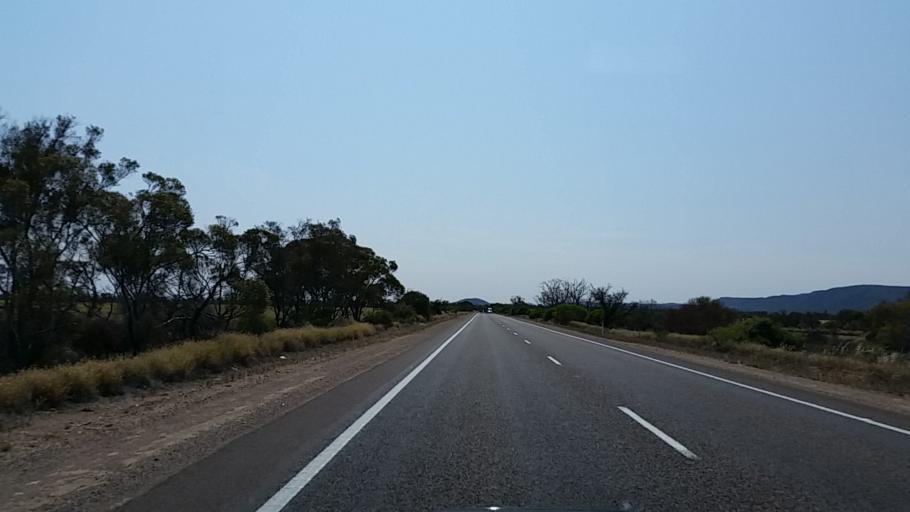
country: AU
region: South Australia
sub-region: Port Pirie City and Dists
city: Port Pirie
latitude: -32.8706
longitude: 137.9822
